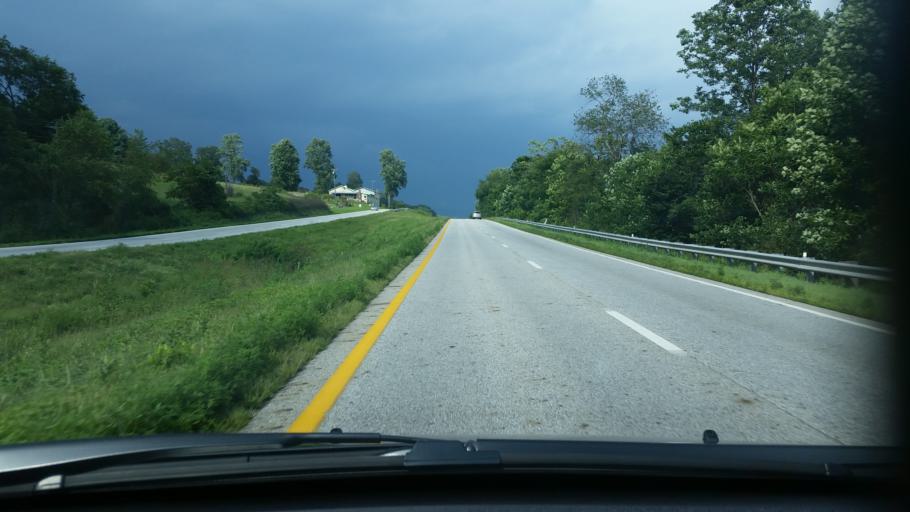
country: US
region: Virginia
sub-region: Nelson County
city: Lovingston
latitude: 37.8107
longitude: -78.8563
